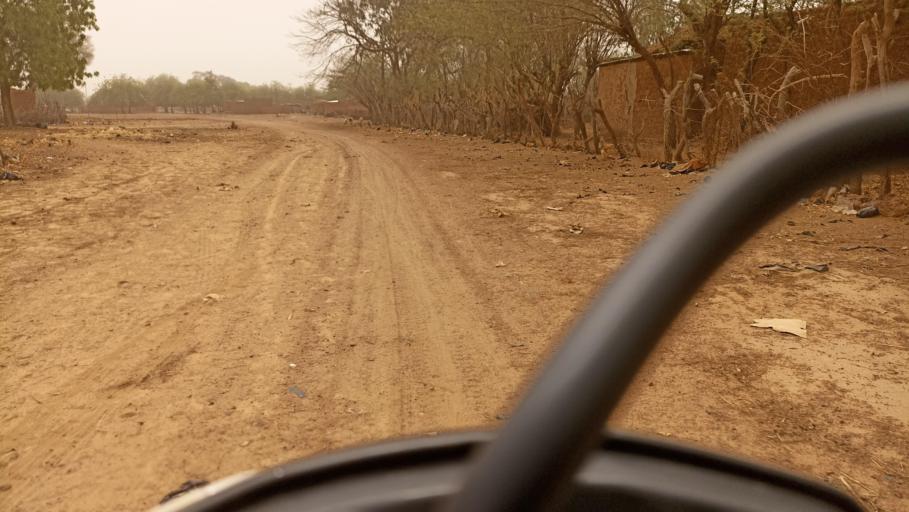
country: BF
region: Nord
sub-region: Province du Zondoma
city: Gourcy
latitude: 13.2482
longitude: -2.5893
